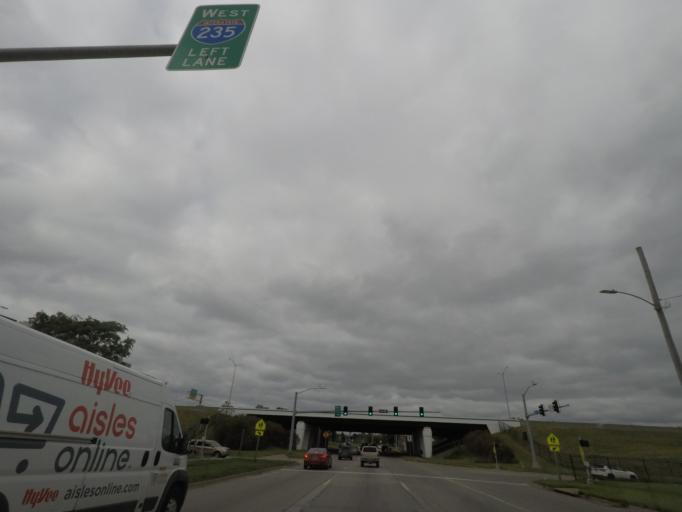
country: US
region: Iowa
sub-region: Polk County
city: Des Moines
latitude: 41.5957
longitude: -93.5960
